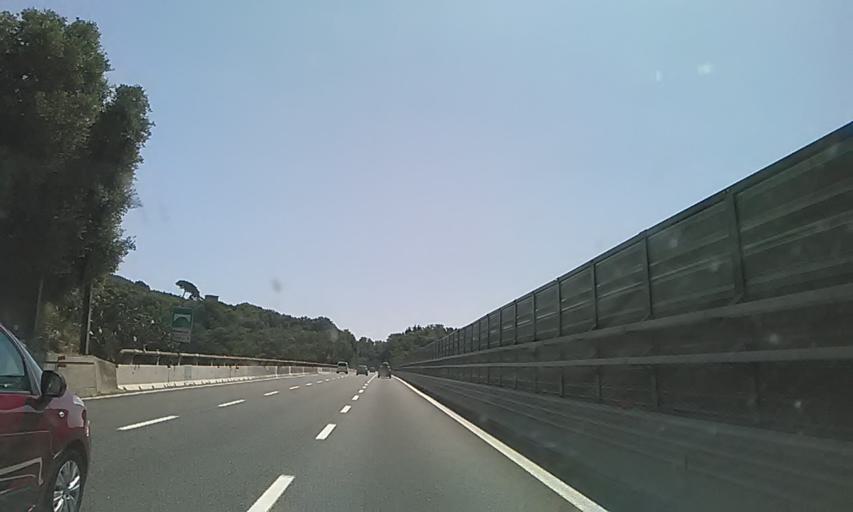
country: IT
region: Liguria
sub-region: Provincia di Savona
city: Varazze
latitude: 44.3637
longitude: 8.5779
